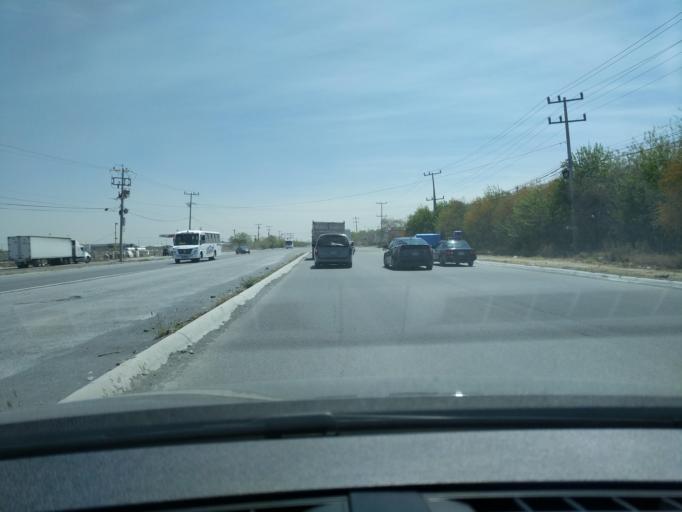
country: MX
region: Nuevo Leon
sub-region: Salinas Victoria
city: Emiliano Zapata
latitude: 25.8905
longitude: -100.2586
